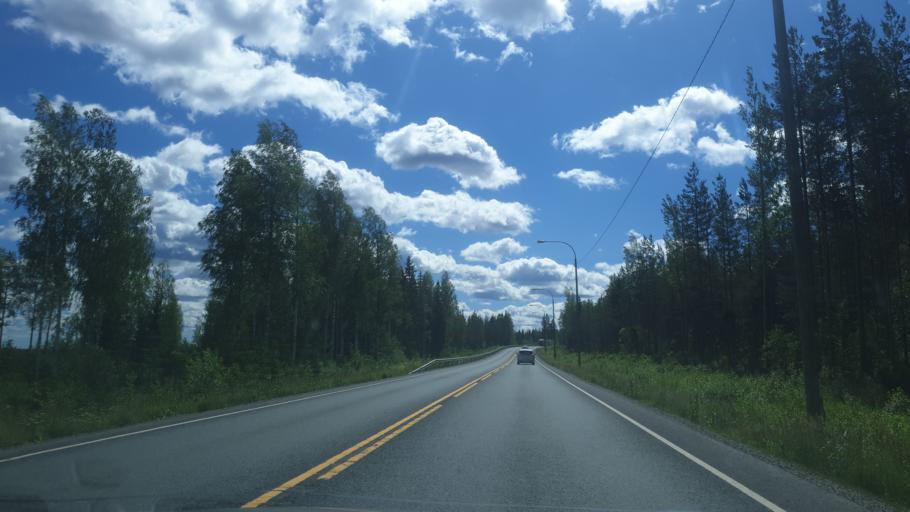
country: FI
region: Northern Savo
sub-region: Varkaus
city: Leppaevirta
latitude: 62.6288
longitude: 27.6187
